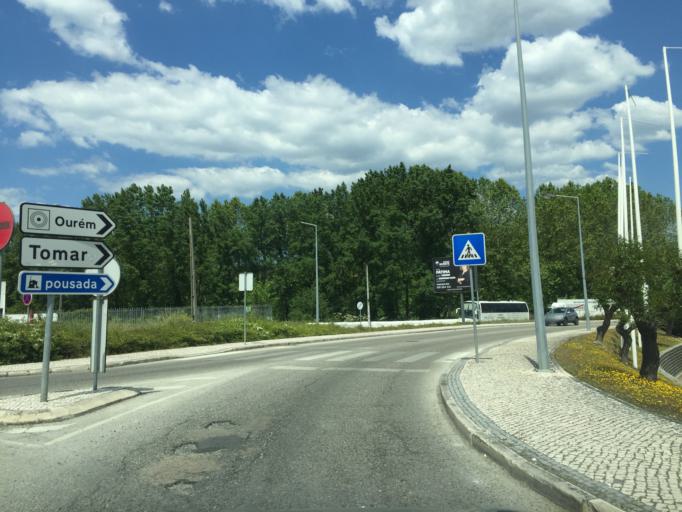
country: PT
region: Santarem
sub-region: Ourem
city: Ourem
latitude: 39.6541
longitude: -8.5916
